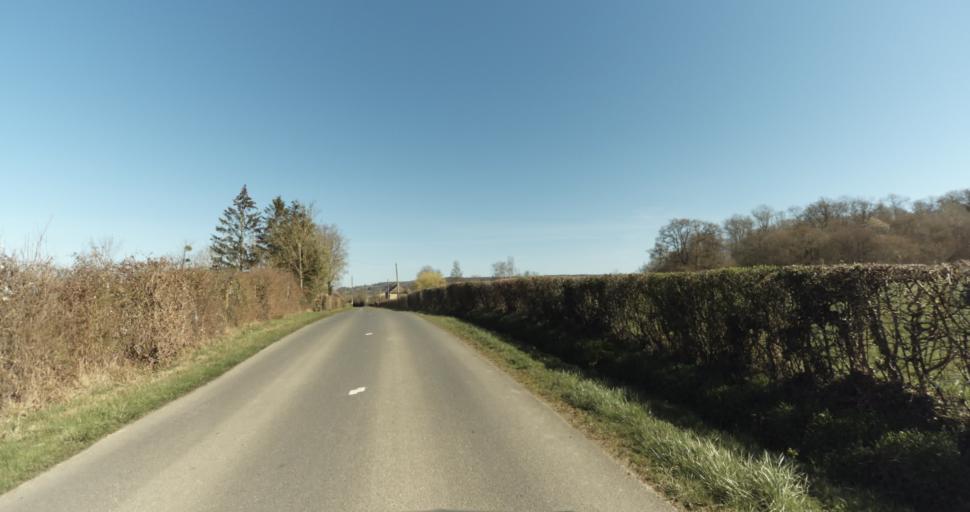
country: FR
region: Lower Normandy
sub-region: Departement du Calvados
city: Saint-Pierre-sur-Dives
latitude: 48.9507
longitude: 0.0478
